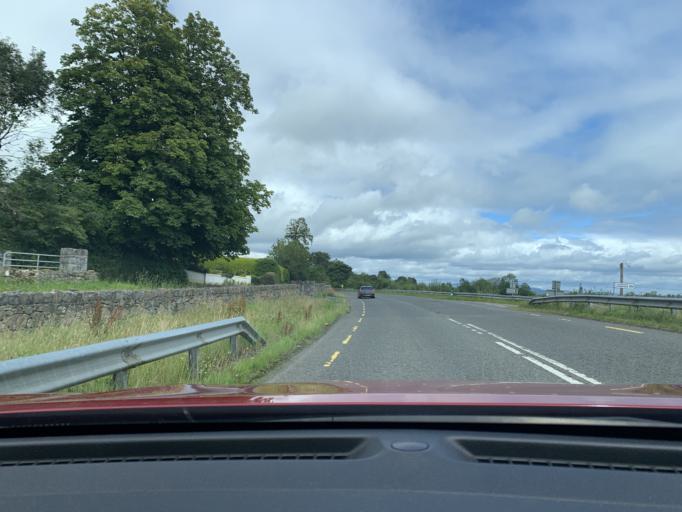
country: IE
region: Connaught
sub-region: County Leitrim
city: Carrick-on-Shannon
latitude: 53.9297
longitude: -8.1097
